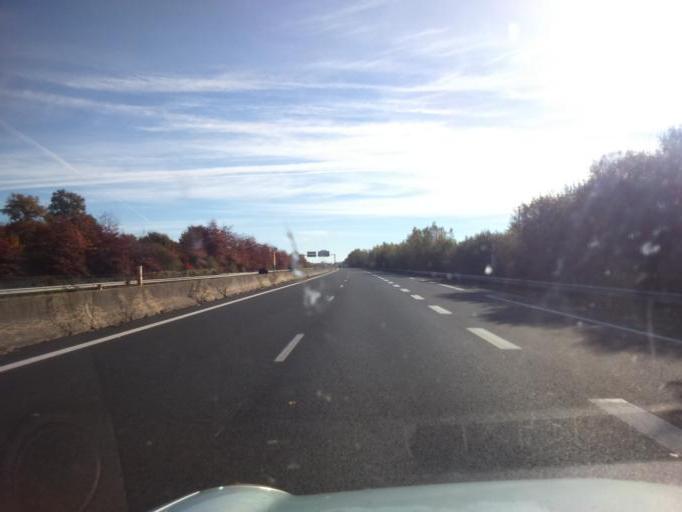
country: FR
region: Poitou-Charentes
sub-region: Departement de la Charente-Maritime
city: Breuil-Magne
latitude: 45.9616
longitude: -0.9570
